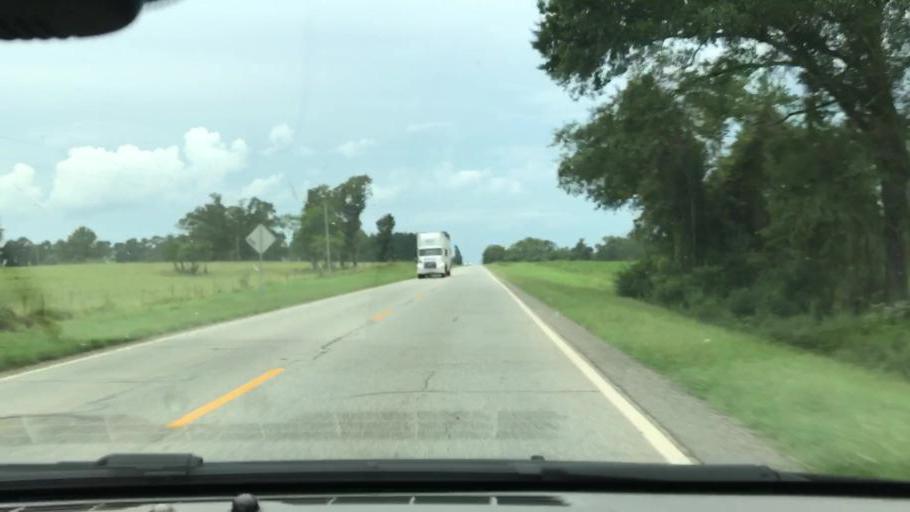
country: US
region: Georgia
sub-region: Early County
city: Blakely
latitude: 31.3292
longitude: -85.0042
